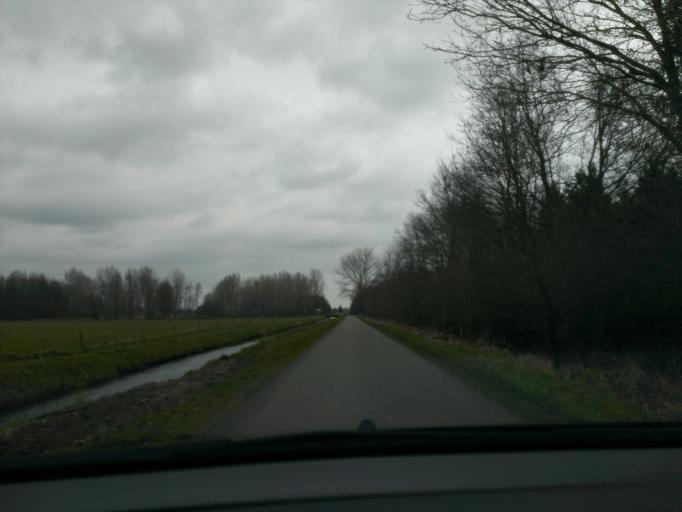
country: NL
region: Gelderland
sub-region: Gemeente Heerde
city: Heerde
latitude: 52.3786
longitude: 6.0543
